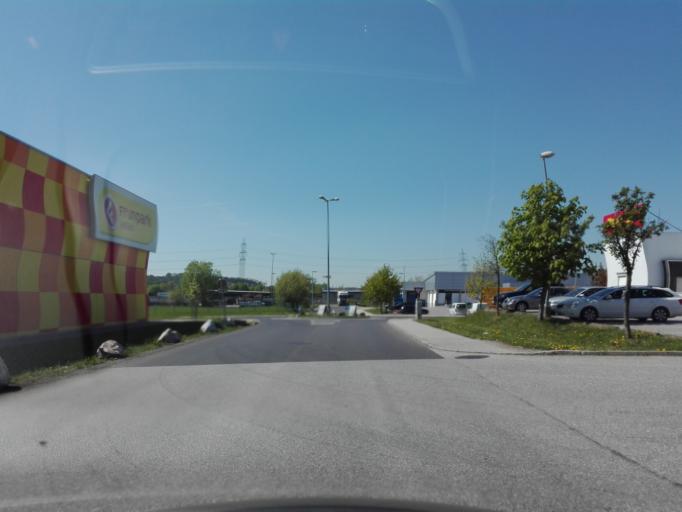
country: AT
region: Upper Austria
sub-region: Politischer Bezirk Linz-Land
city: Asten
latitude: 48.2219
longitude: 14.4060
